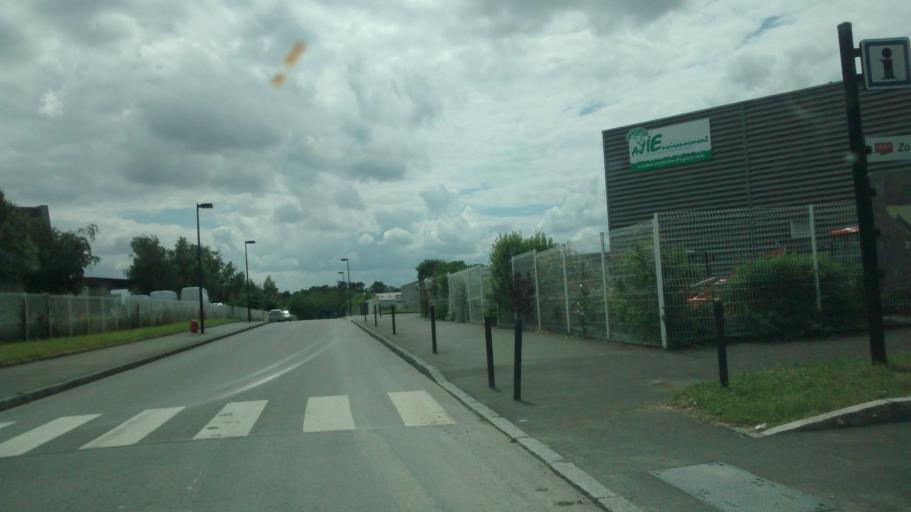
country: FR
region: Brittany
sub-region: Departement d'Ille-et-Vilaine
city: Saint-Jacques-de-la-Lande
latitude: 48.0683
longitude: -1.7000
